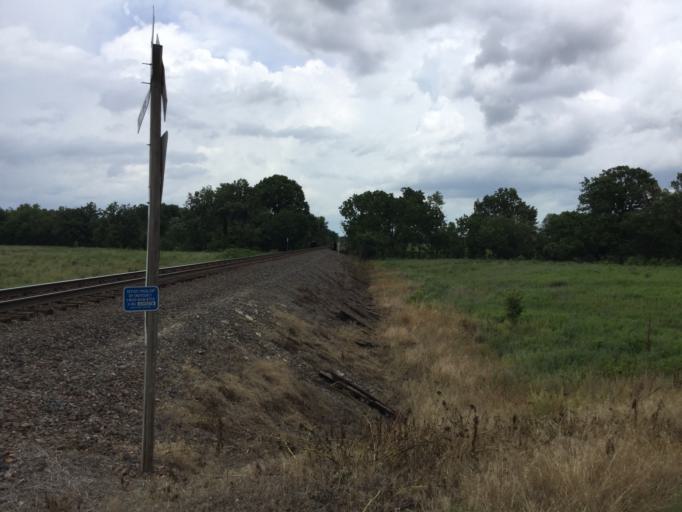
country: US
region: Kansas
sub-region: Woodson County
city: Yates Center
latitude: 37.9662
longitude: -95.6712
